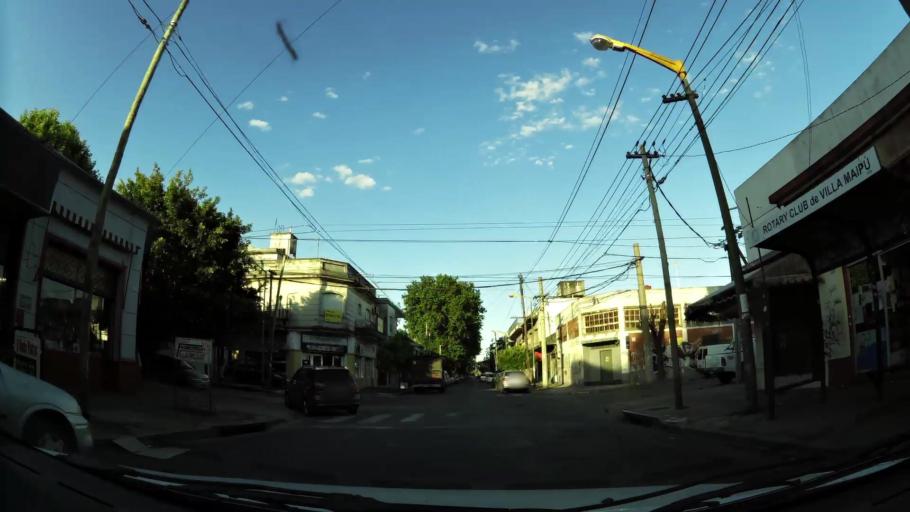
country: AR
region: Buenos Aires
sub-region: Partido de General San Martin
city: General San Martin
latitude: -34.5691
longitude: -58.5223
